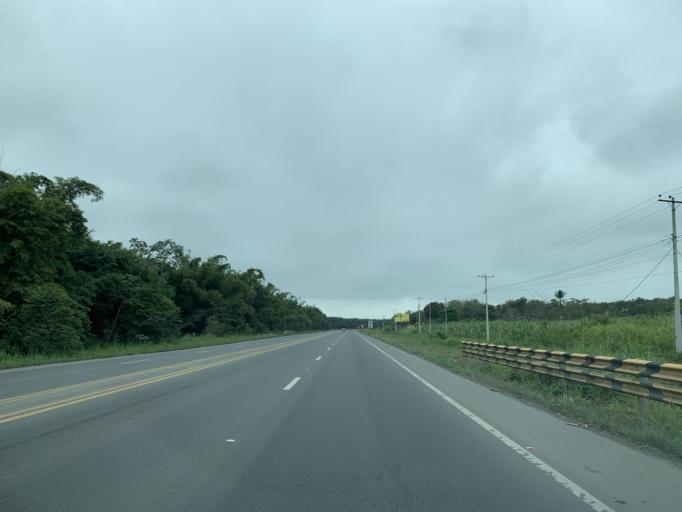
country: EC
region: Guayas
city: Coronel Marcelino Mariduena
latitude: -2.3247
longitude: -79.4519
